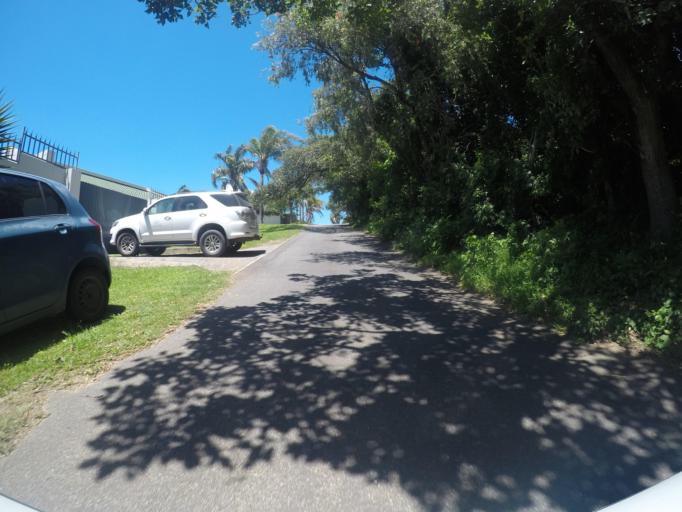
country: ZA
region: Eastern Cape
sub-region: Buffalo City Metropolitan Municipality
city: East London
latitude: -32.9318
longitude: 27.9934
